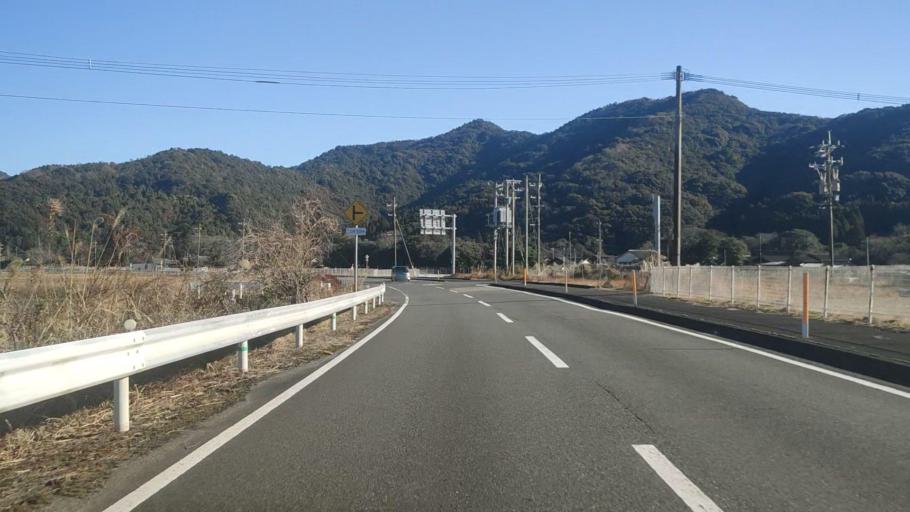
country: JP
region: Miyazaki
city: Nobeoka
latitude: 32.6791
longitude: 131.7850
